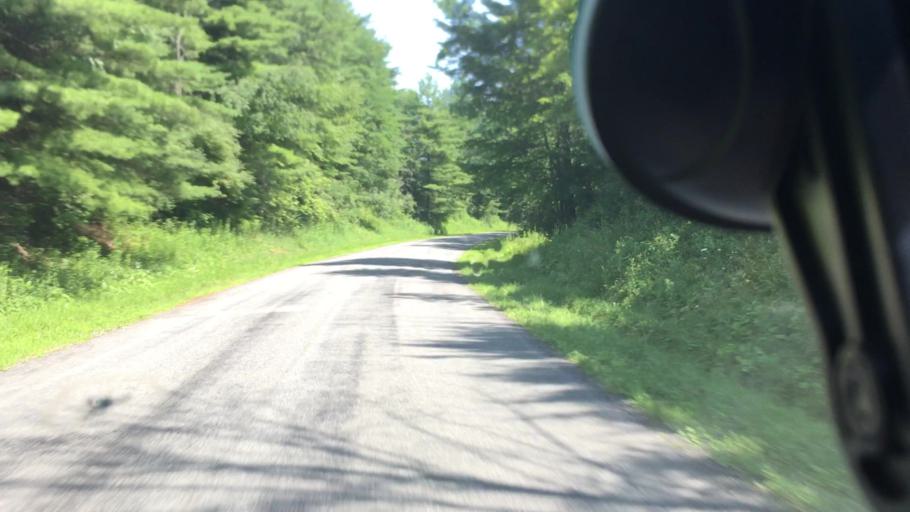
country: US
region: Ohio
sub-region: Columbiana County
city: Lisbon
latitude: 40.7664
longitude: -80.7922
